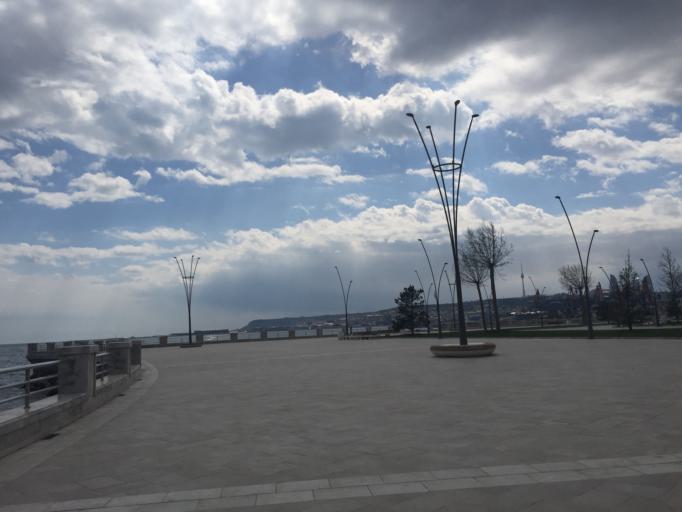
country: AZ
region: Baki
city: Baku
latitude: 40.3743
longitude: 49.8716
